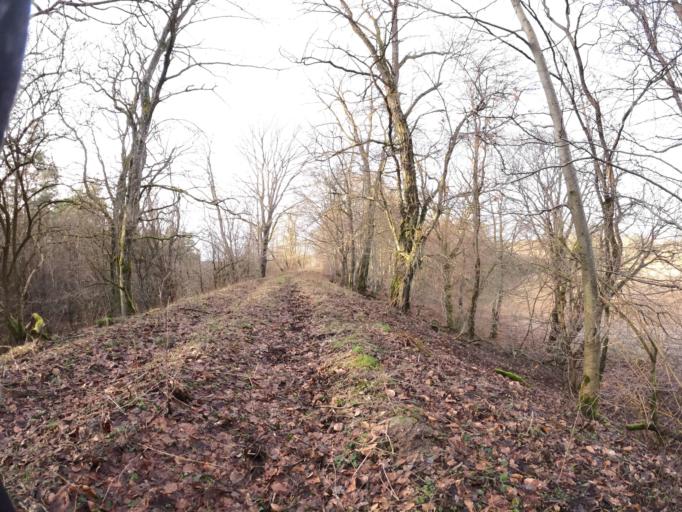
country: PL
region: West Pomeranian Voivodeship
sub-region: Powiat koszalinski
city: Polanow
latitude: 54.1773
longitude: 16.7328
